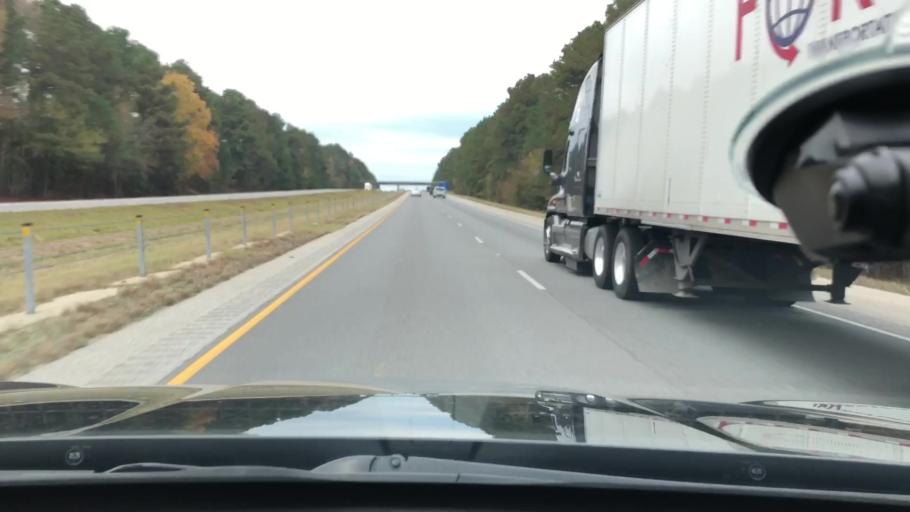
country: US
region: Arkansas
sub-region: Clark County
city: Arkadelphia
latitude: 34.0885
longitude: -93.1106
